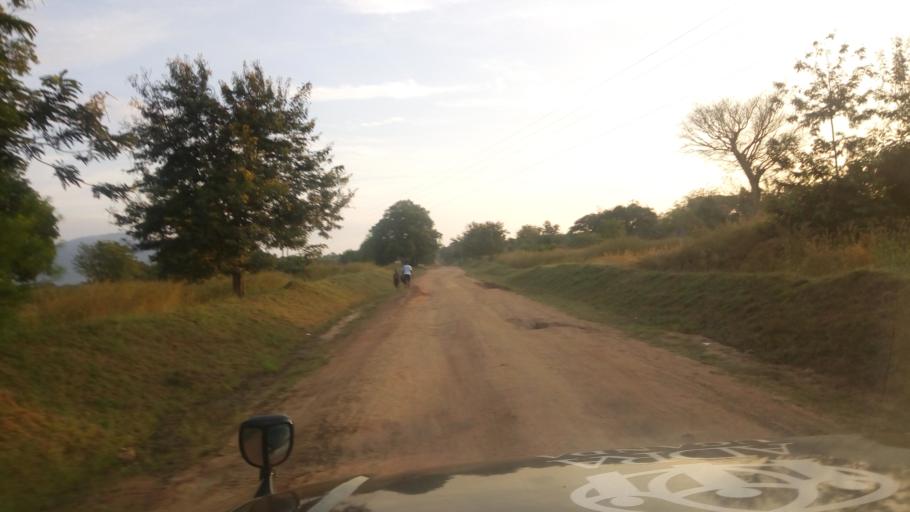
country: UG
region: Northern Region
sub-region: Adjumani District
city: Adjumani
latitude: 3.5267
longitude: 31.8059
